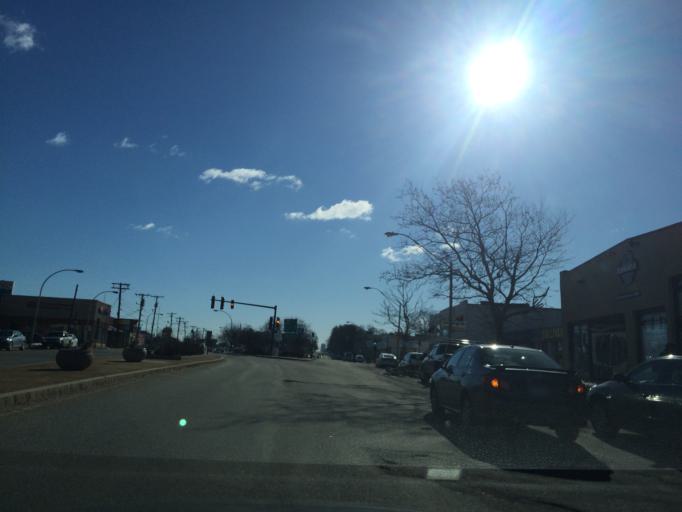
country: US
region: Massachusetts
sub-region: Middlesex County
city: Watertown
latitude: 42.3650
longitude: -71.1834
